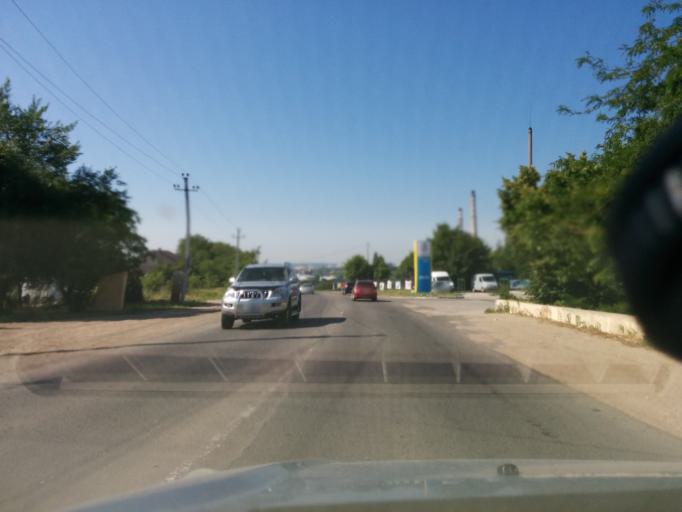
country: MD
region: Chisinau
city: Chisinau
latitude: 47.0414
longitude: 28.9050
